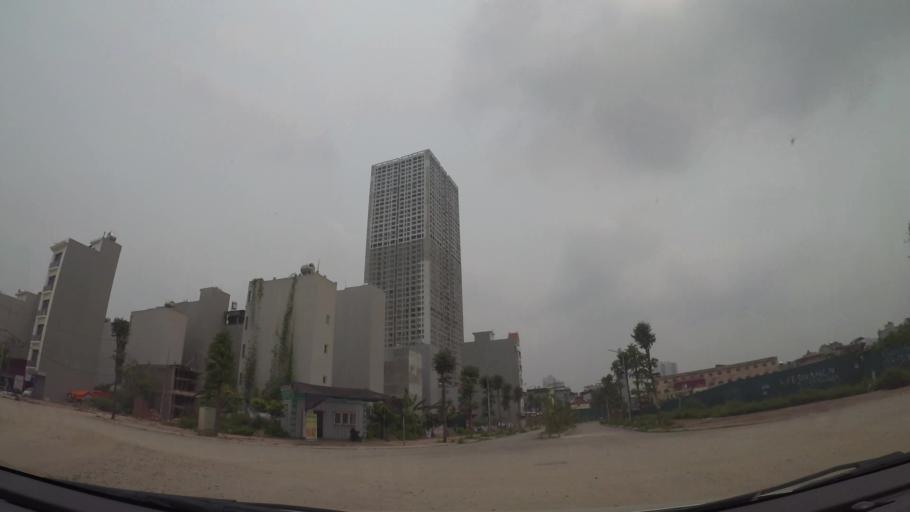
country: VN
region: Ha Noi
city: Ha Dong
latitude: 20.9793
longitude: 105.7696
